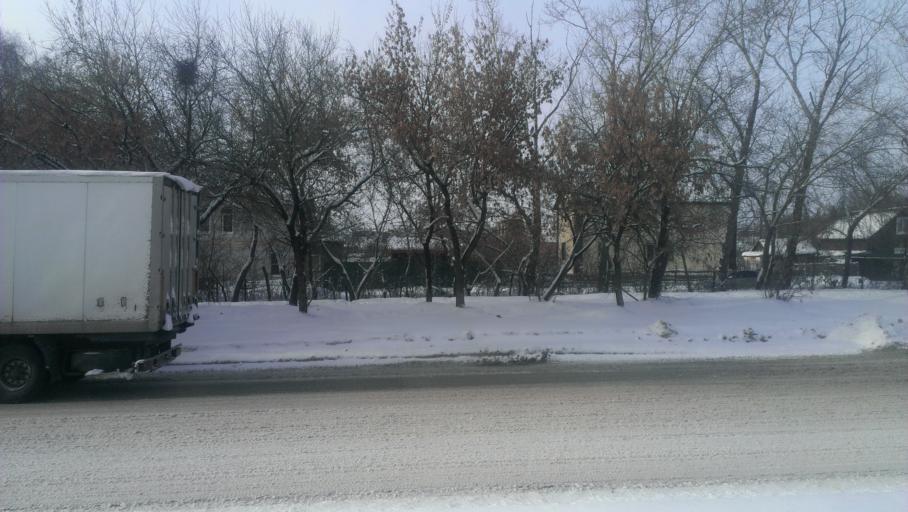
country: RU
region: Altai Krai
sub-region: Gorod Barnaulskiy
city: Barnaul
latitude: 53.3864
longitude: 83.6840
